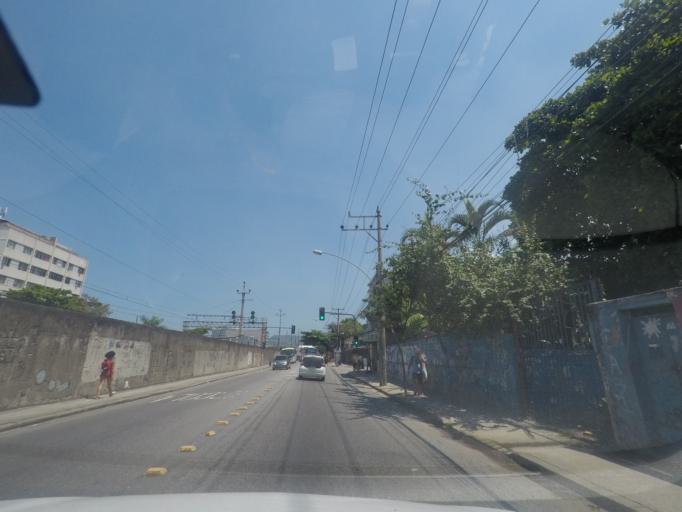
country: BR
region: Rio de Janeiro
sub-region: Rio De Janeiro
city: Rio de Janeiro
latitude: -22.8609
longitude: -43.2578
